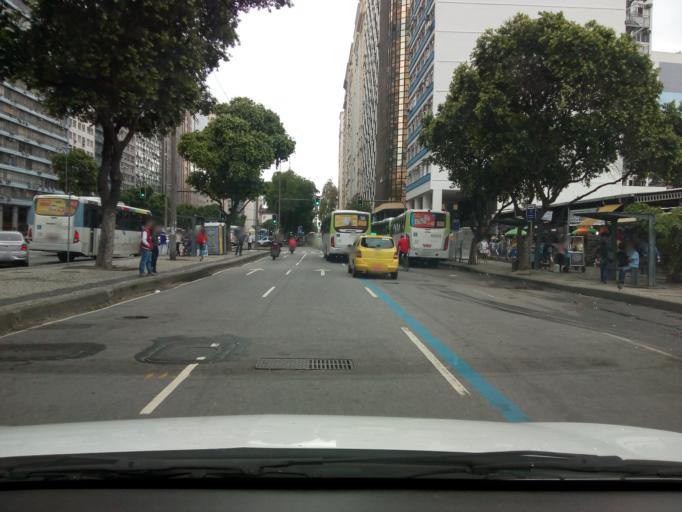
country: BR
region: Rio de Janeiro
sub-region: Rio De Janeiro
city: Rio de Janeiro
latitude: -22.9025
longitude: -43.1823
